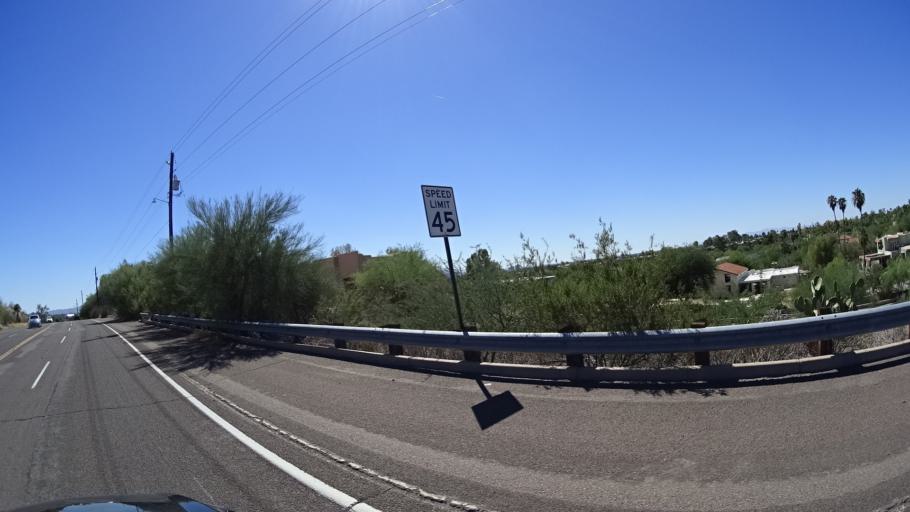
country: US
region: Arizona
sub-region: Maricopa County
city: Paradise Valley
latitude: 33.5229
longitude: -112.0132
